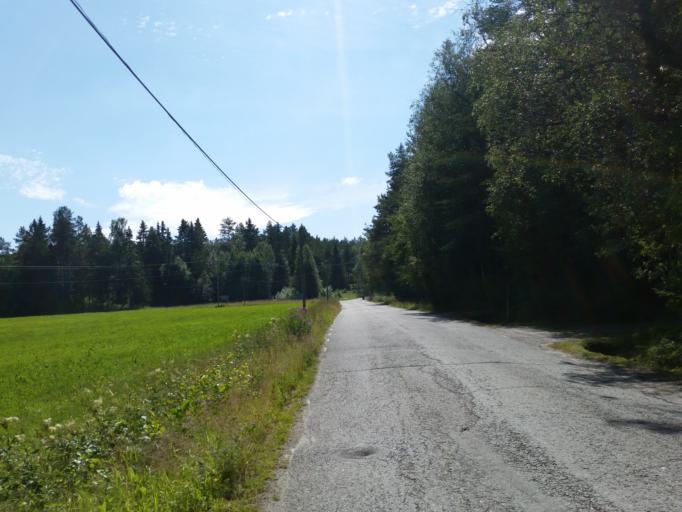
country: SE
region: Vaesterbotten
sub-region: Robertsfors Kommun
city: Robertsfors
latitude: 64.0411
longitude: 20.8577
